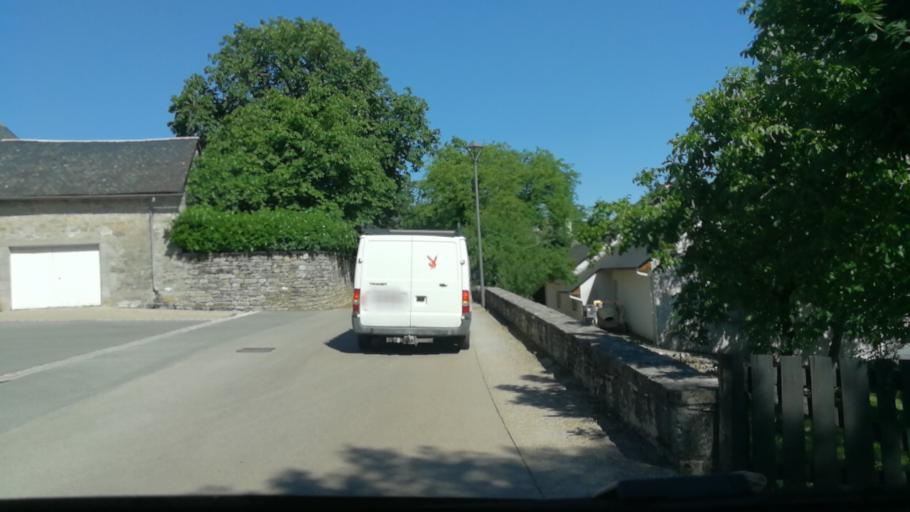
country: FR
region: Midi-Pyrenees
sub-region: Departement de l'Aveyron
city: Sebazac-Concoures
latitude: 44.4194
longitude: 2.5638
